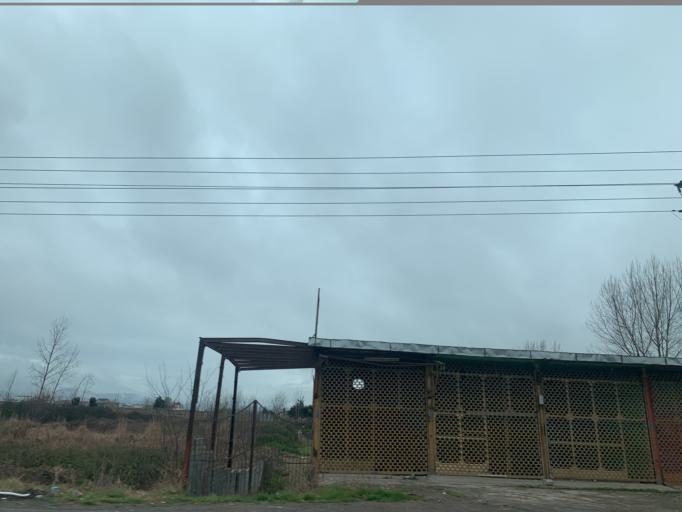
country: IR
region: Mazandaran
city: Amol
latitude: 36.4201
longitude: 52.3495
